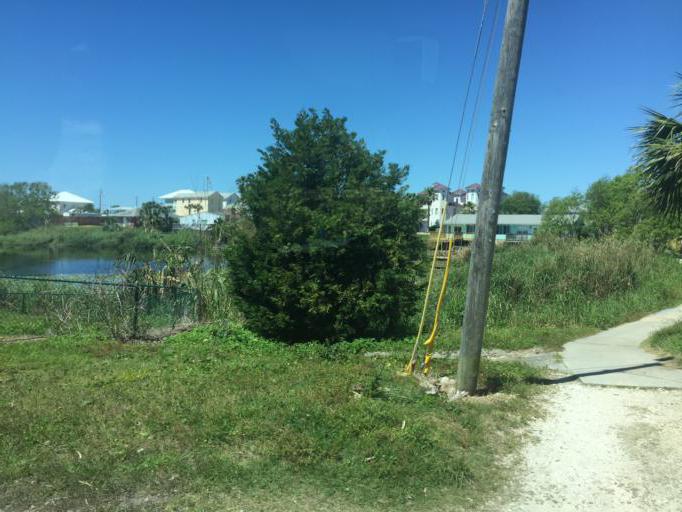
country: US
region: Florida
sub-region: Bay County
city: Laguna Beach
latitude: 30.2444
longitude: -85.9305
